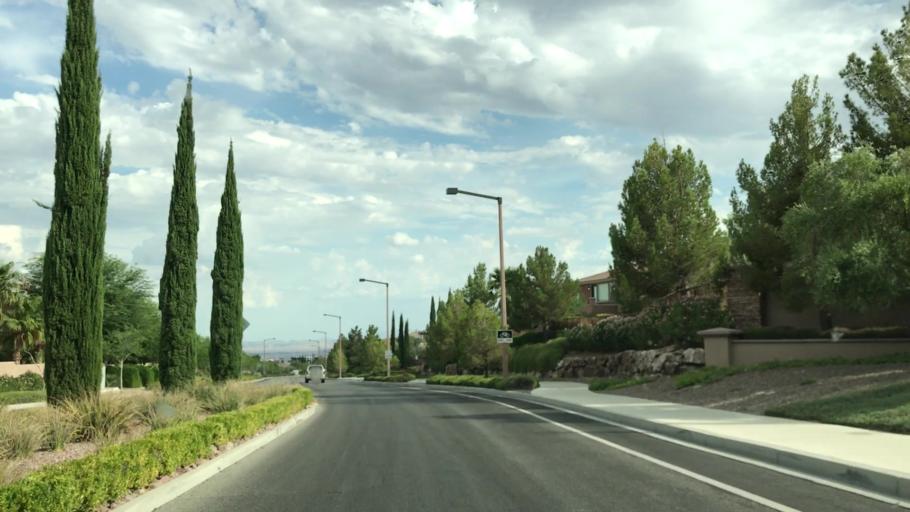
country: US
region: Nevada
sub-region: Clark County
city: Summerlin South
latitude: 36.1719
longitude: -115.3520
